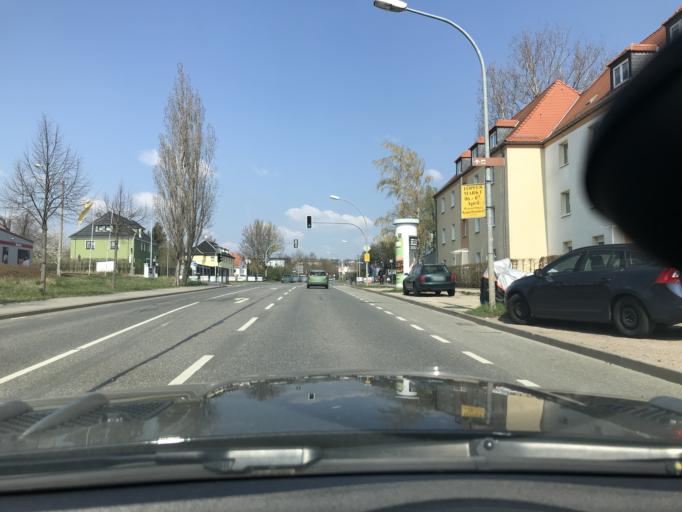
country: DE
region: Thuringia
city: Weimar
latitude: 50.9987
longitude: 11.3327
